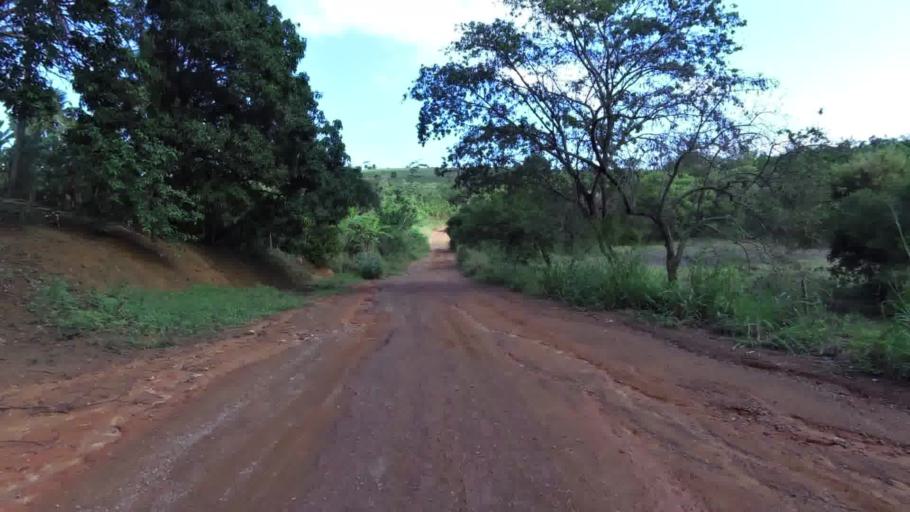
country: BR
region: Espirito Santo
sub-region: Piuma
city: Piuma
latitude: -20.8173
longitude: -40.6763
